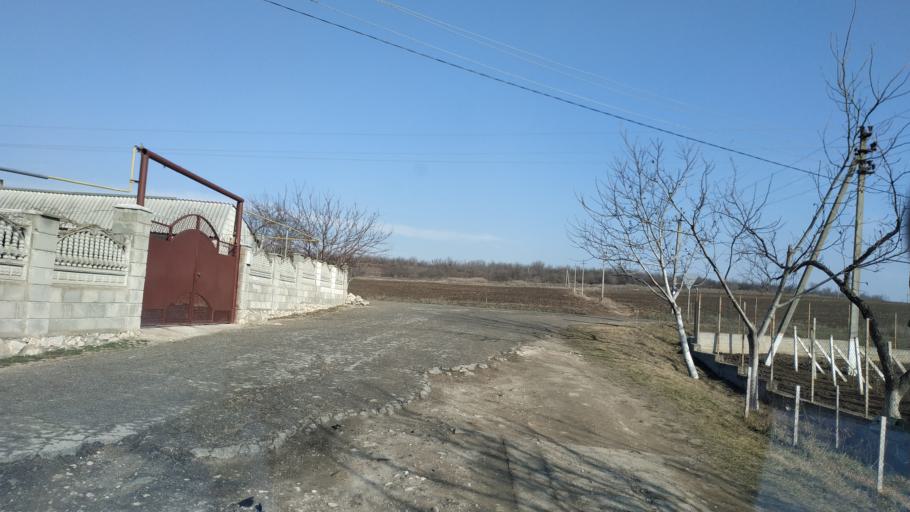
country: MD
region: Chisinau
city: Singera
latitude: 46.6884
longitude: 29.0411
